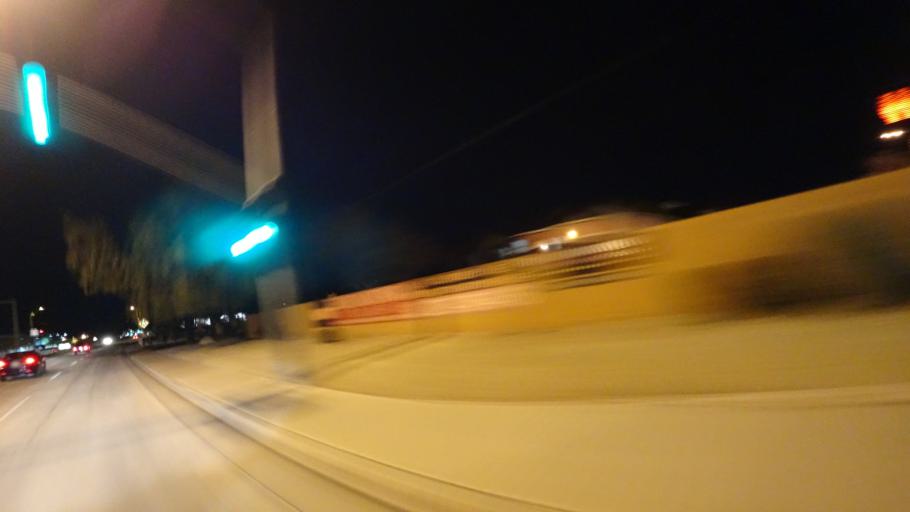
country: US
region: Arizona
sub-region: Maricopa County
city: Tempe Junction
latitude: 33.4552
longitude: -111.9696
